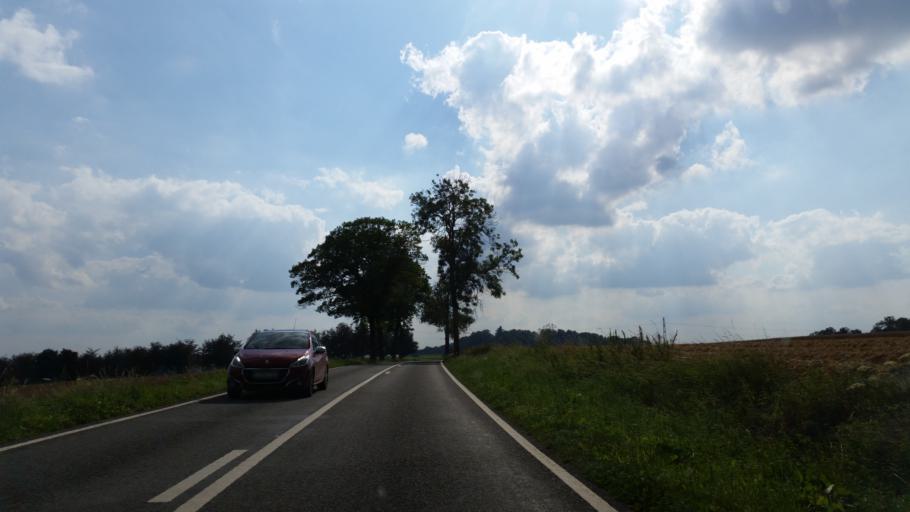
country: BE
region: Wallonia
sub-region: Province de Liege
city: Anthisnes
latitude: 50.4804
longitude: 5.4946
